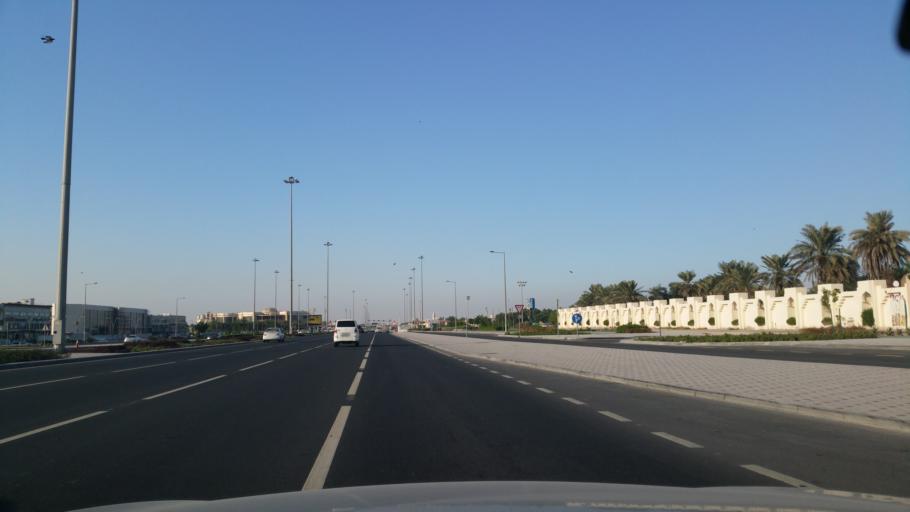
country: QA
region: Baladiyat ar Rayyan
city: Ar Rayyan
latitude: 25.2647
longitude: 51.4314
